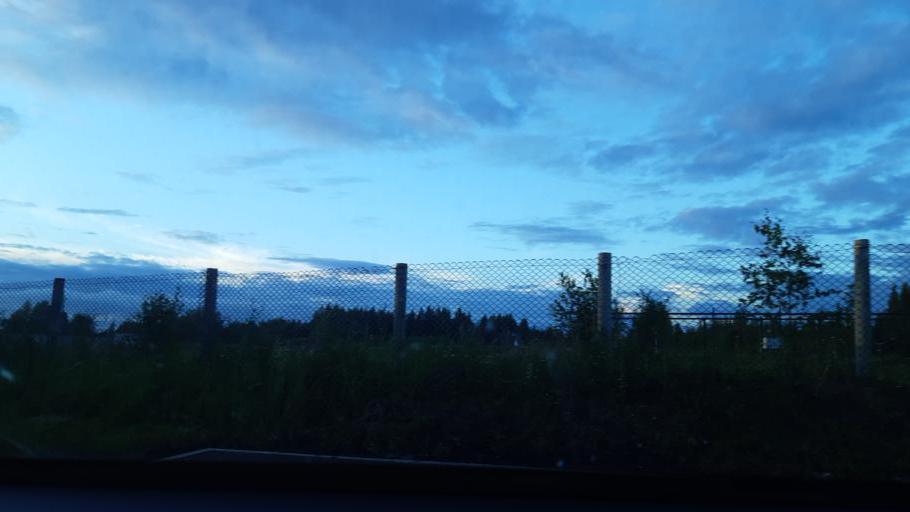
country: RU
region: Smolensk
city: Safonovo
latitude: 55.1270
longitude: 33.2008
